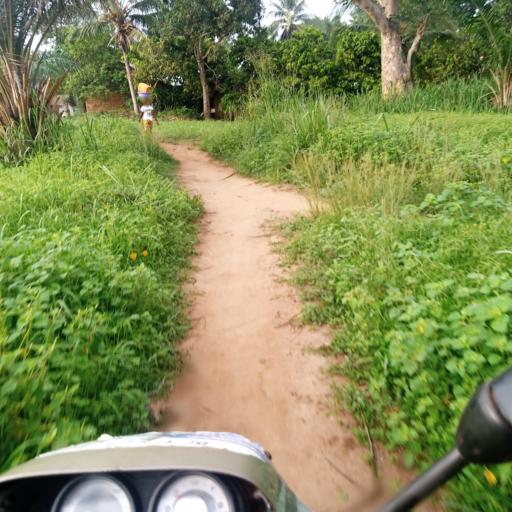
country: SL
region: Eastern Province
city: Pendembu
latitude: 8.0991
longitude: -10.6919
